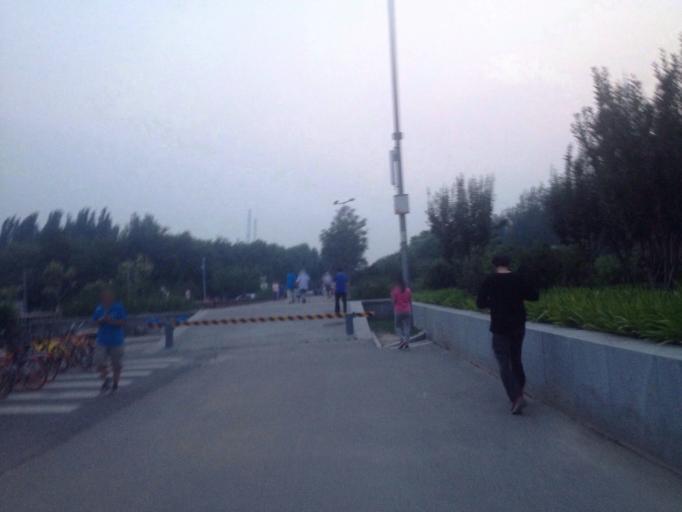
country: CN
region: Beijing
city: Datun
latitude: 40.0082
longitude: 116.3919
